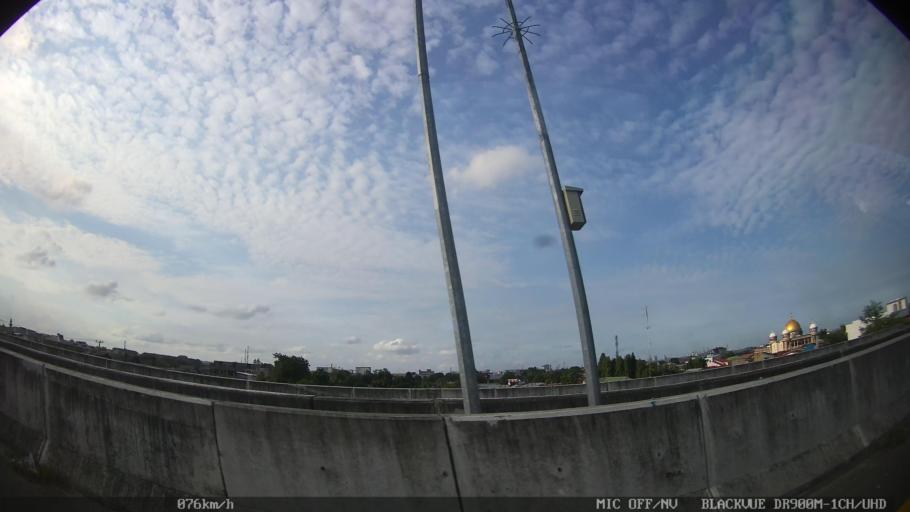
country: ID
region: North Sumatra
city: Medan
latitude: 3.6475
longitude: 98.6723
